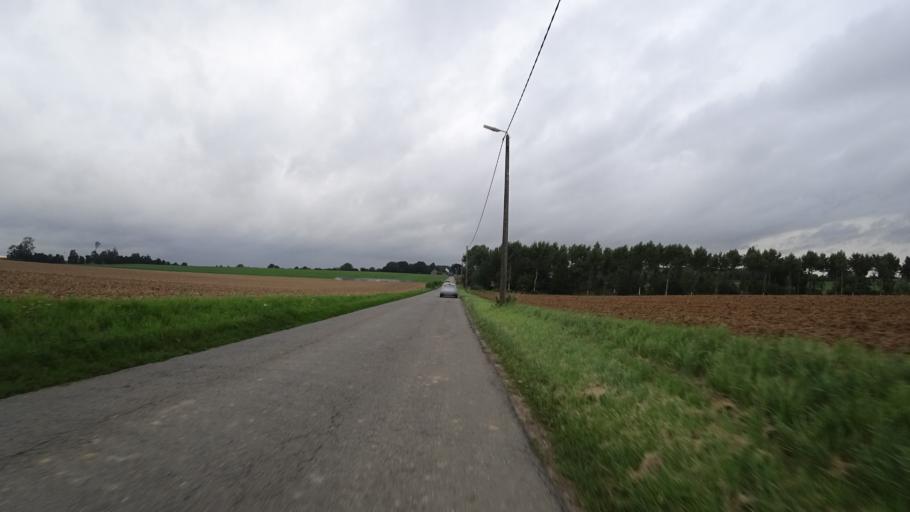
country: BE
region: Wallonia
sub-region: Province du Brabant Wallon
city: Walhain-Saint-Paul
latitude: 50.5980
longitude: 4.7527
